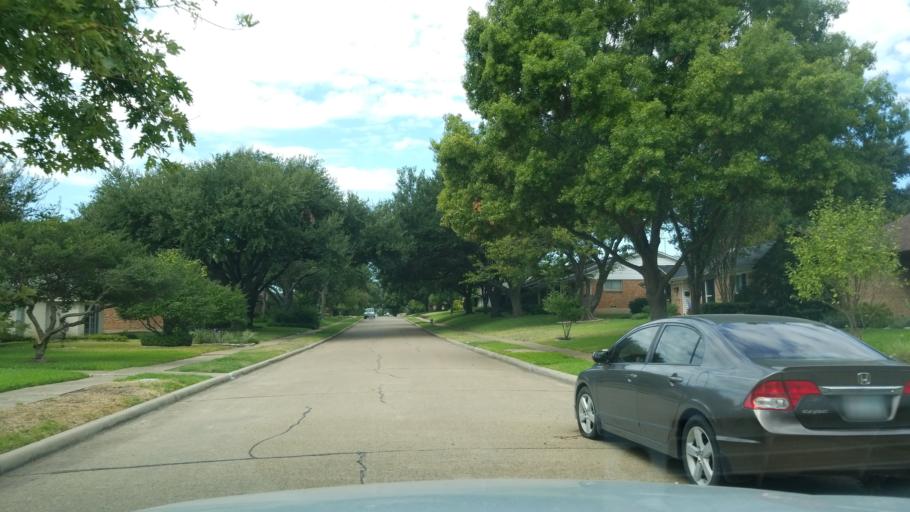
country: US
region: Texas
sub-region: Dallas County
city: Richardson
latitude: 32.9652
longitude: -96.7737
